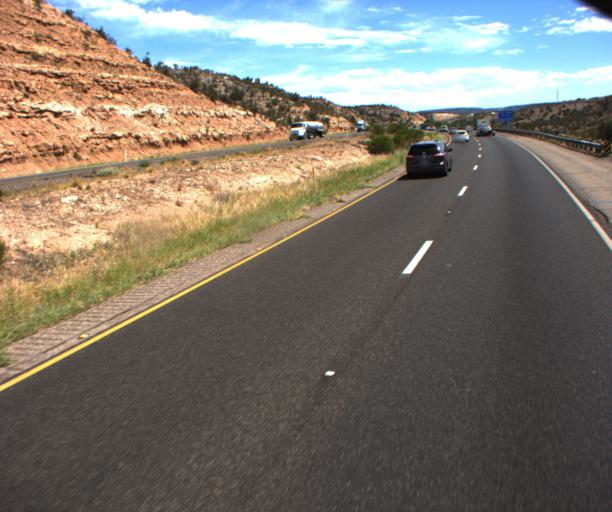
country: US
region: Arizona
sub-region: Yavapai County
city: Lake Montezuma
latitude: 34.6617
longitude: -111.7868
